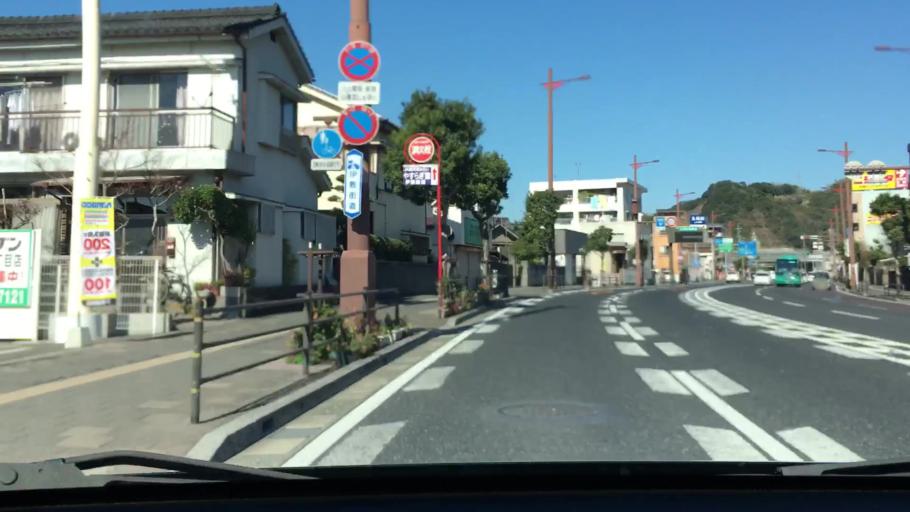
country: JP
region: Kagoshima
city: Kagoshima-shi
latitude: 31.6204
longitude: 130.5264
